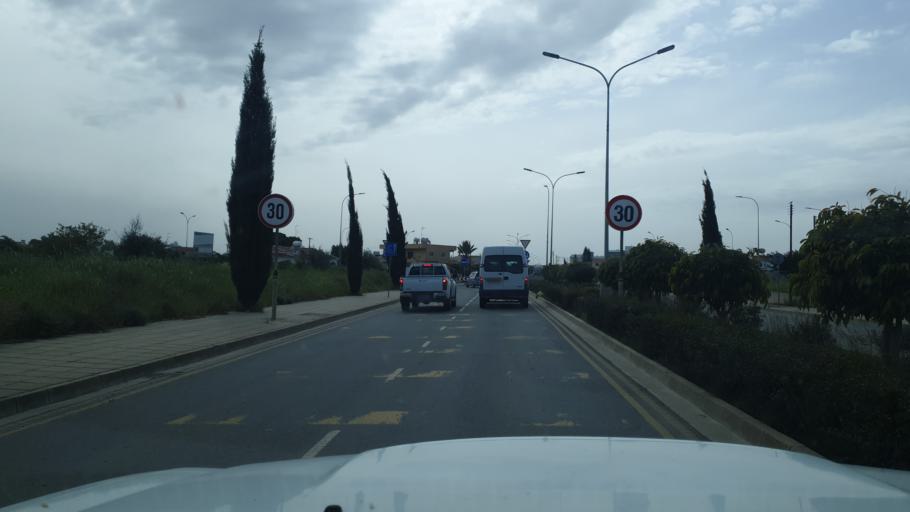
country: CY
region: Lefkosia
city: Tseri
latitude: 35.1128
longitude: 33.3124
